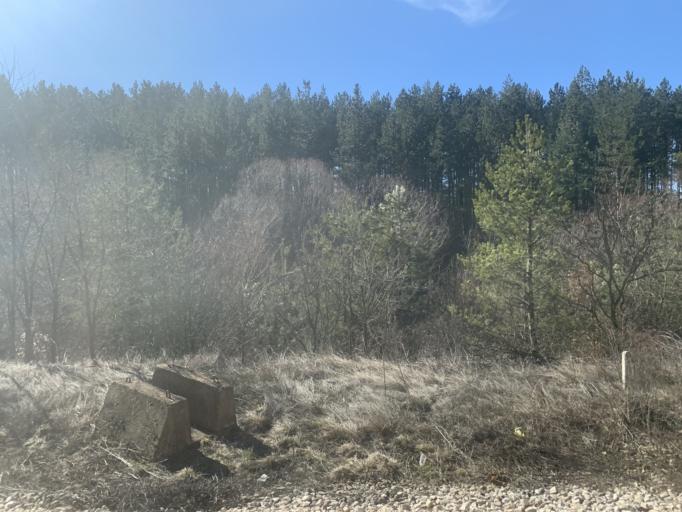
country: BG
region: Sofiya
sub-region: Obshtina Gorna Malina
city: Gorna Malina
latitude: 42.5648
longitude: 23.6837
